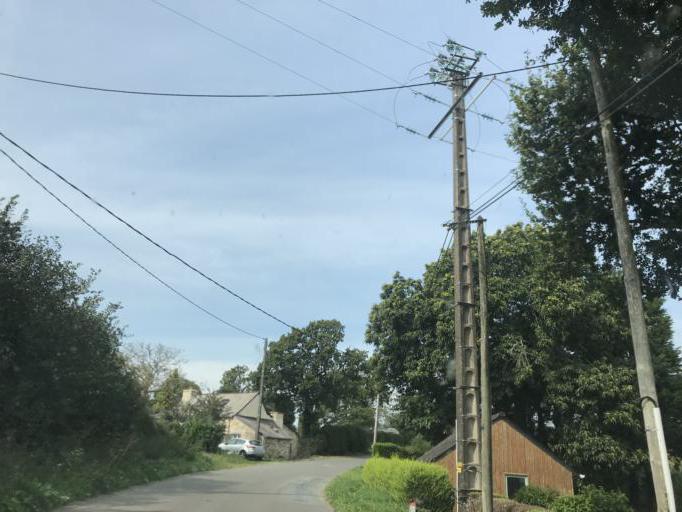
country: FR
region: Brittany
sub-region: Departement du Finistere
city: Brasparts
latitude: 48.3167
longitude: -3.9323
